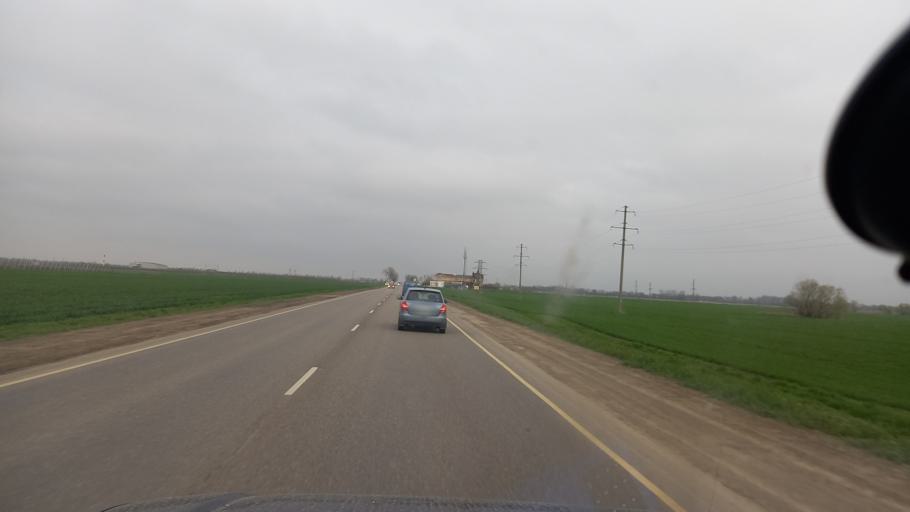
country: RU
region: Krasnodarskiy
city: Slavyansk-na-Kubani
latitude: 45.2419
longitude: 38.0305
